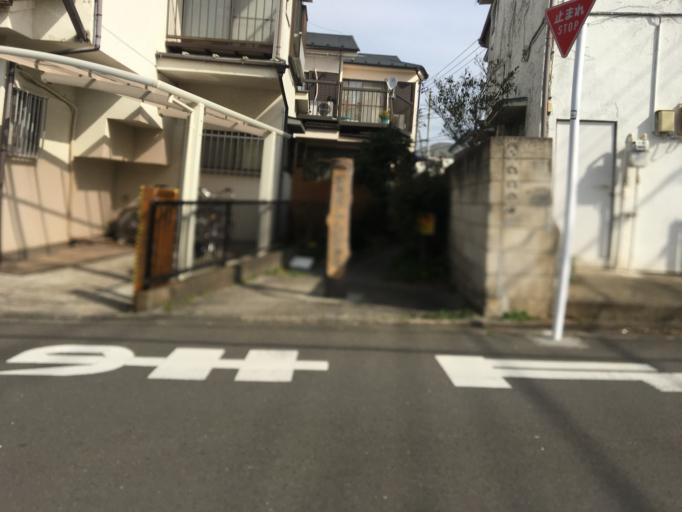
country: JP
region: Tokyo
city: Kokubunji
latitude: 35.6923
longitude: 139.5109
